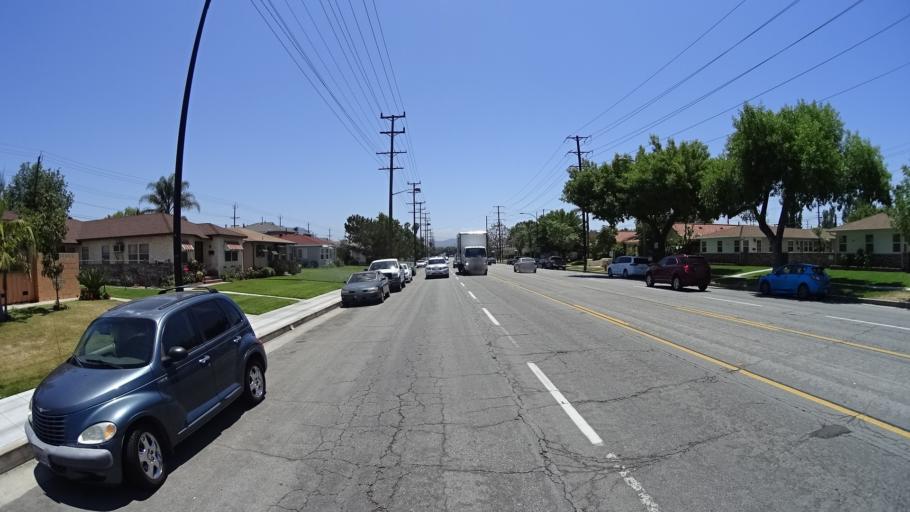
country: US
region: California
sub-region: Los Angeles County
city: North Hollywood
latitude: 34.1790
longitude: -118.3494
